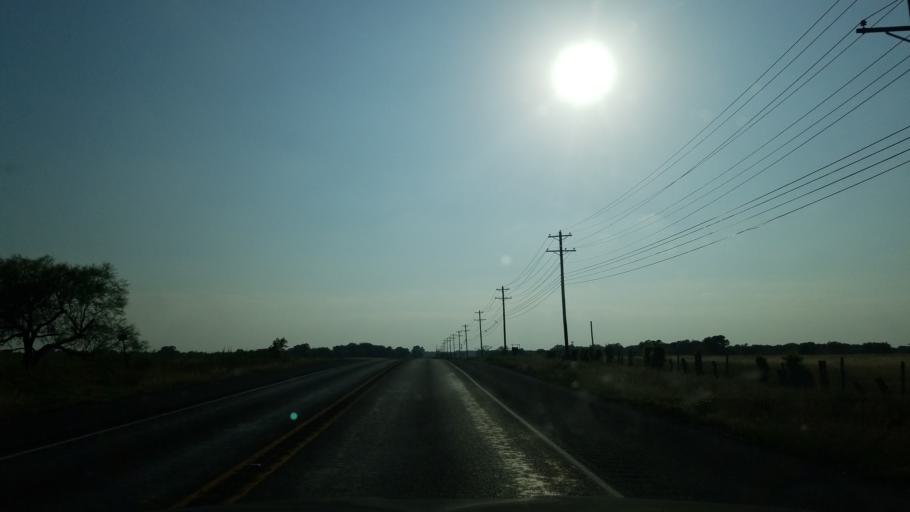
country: US
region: Texas
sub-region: Denton County
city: Aubrey
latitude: 33.3072
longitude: -97.0515
